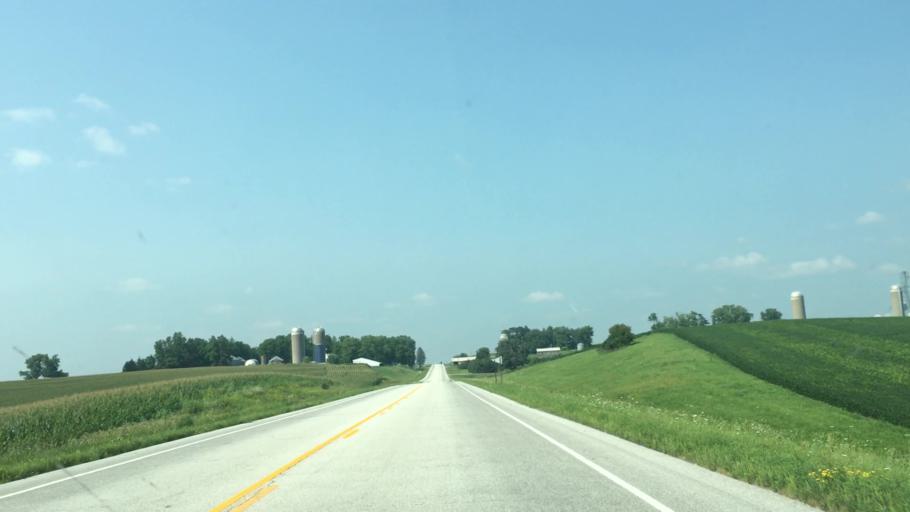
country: US
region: Minnesota
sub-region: Fillmore County
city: Harmony
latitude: 43.6105
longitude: -91.9298
